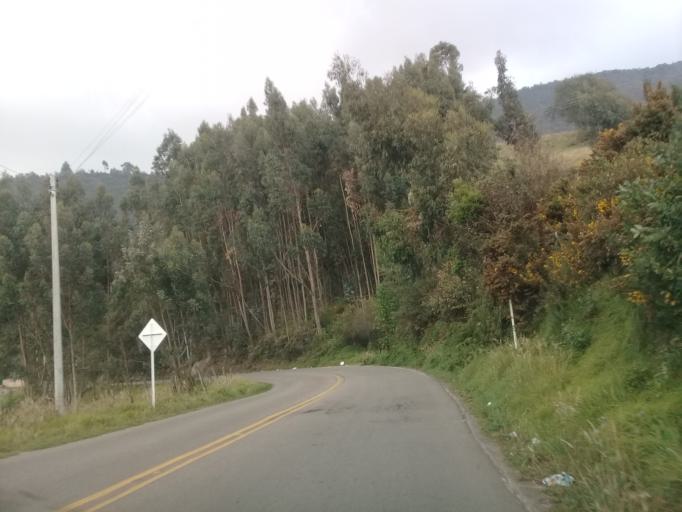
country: CO
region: Cundinamarca
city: Zipaquira
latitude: 5.0386
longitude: -74.0454
